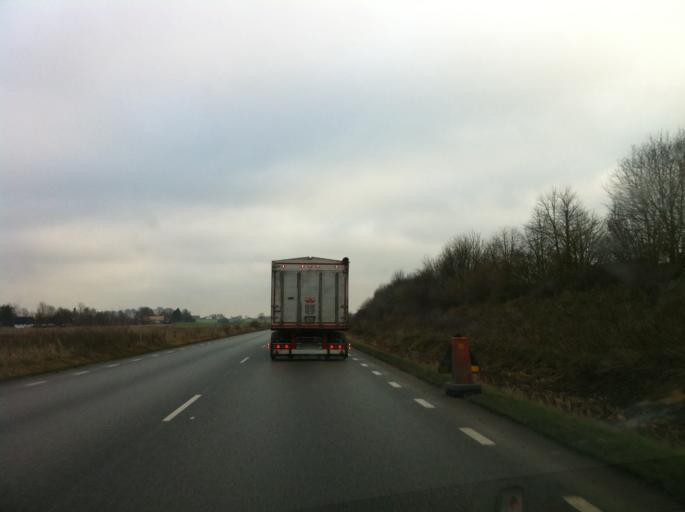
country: SE
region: Skane
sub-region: Kavlinge Kommun
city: Kaevlinge
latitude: 55.7982
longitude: 13.1341
